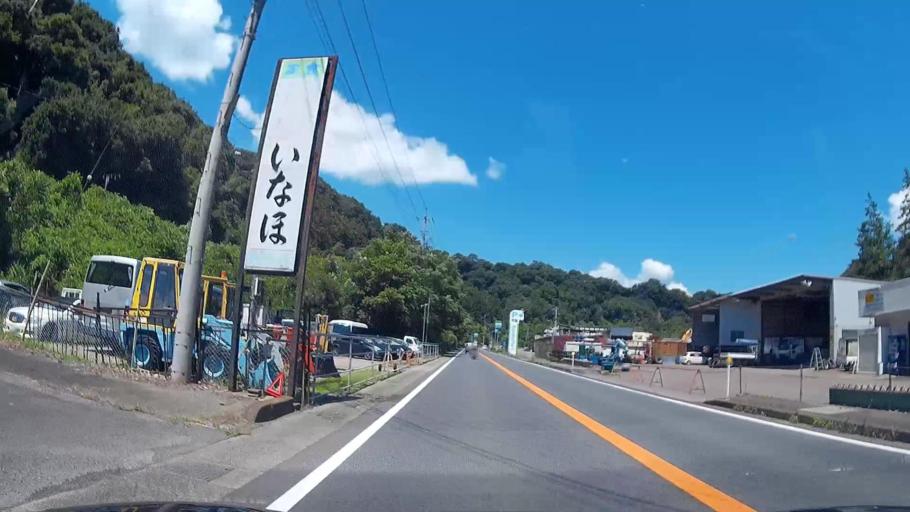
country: JP
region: Gunma
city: Numata
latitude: 36.6223
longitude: 139.0381
